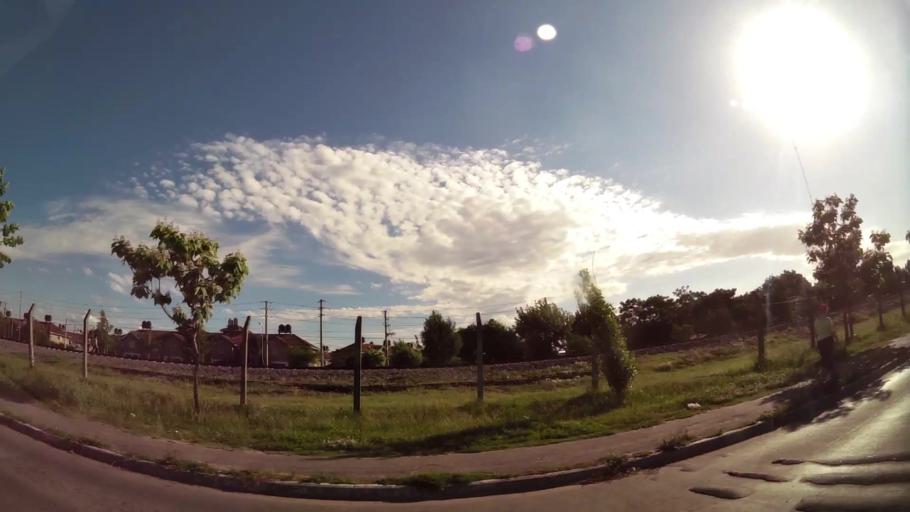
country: AR
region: Buenos Aires
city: Santa Catalina - Dique Lujan
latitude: -34.4898
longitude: -58.7148
